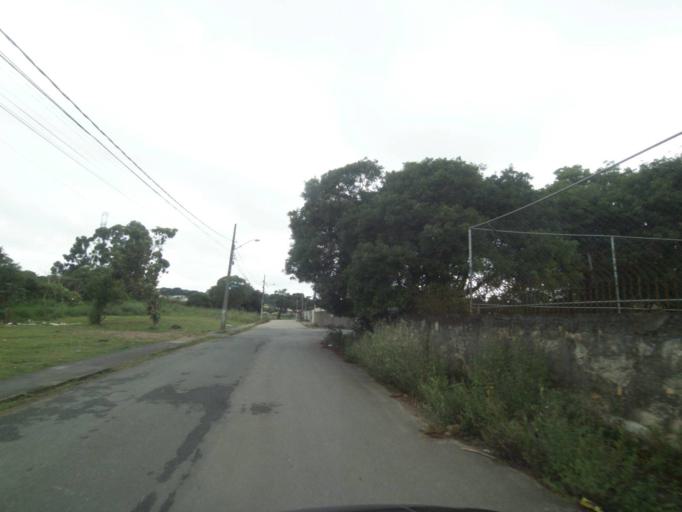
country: BR
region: Parana
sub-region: Curitiba
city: Curitiba
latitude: -25.4669
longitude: -49.3213
